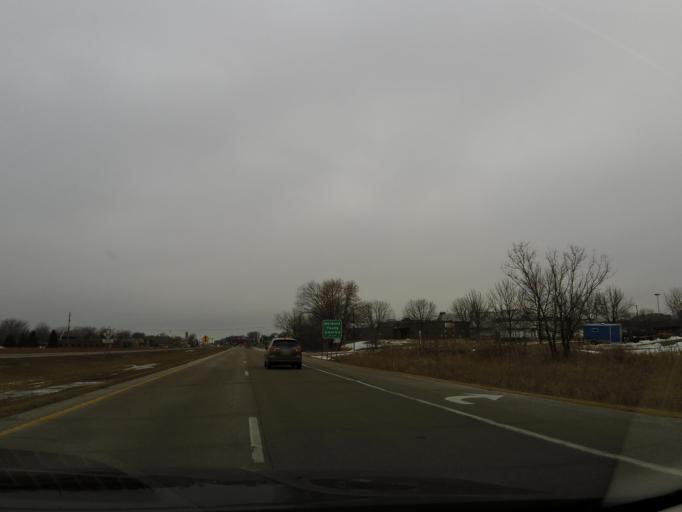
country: US
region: Minnesota
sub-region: Carver County
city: Norwood Young America
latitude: 44.7699
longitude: -93.9147
